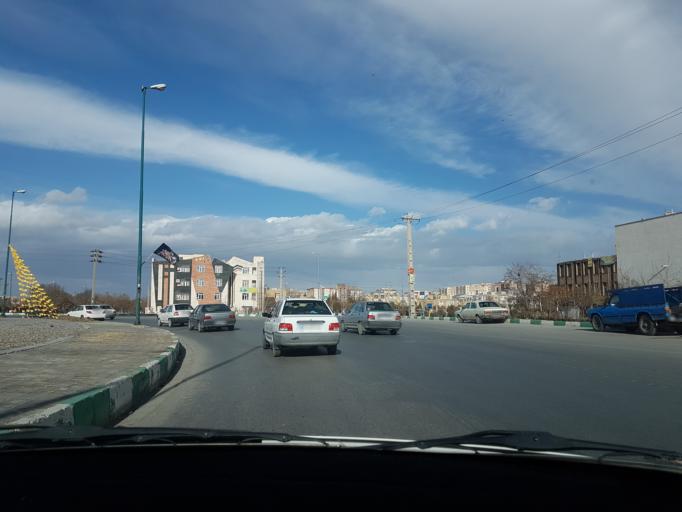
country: IR
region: Markazi
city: Arak
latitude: 34.1190
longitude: 49.7056
